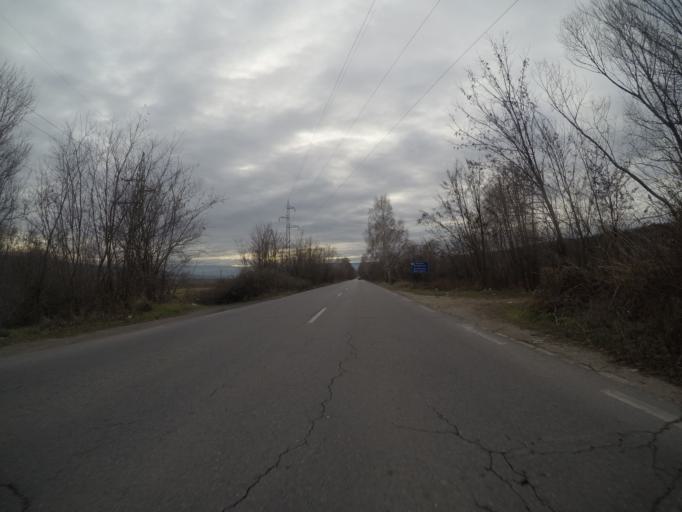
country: BG
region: Kyustendil
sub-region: Obshtina Rila
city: Rila
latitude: 42.1095
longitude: 23.1047
